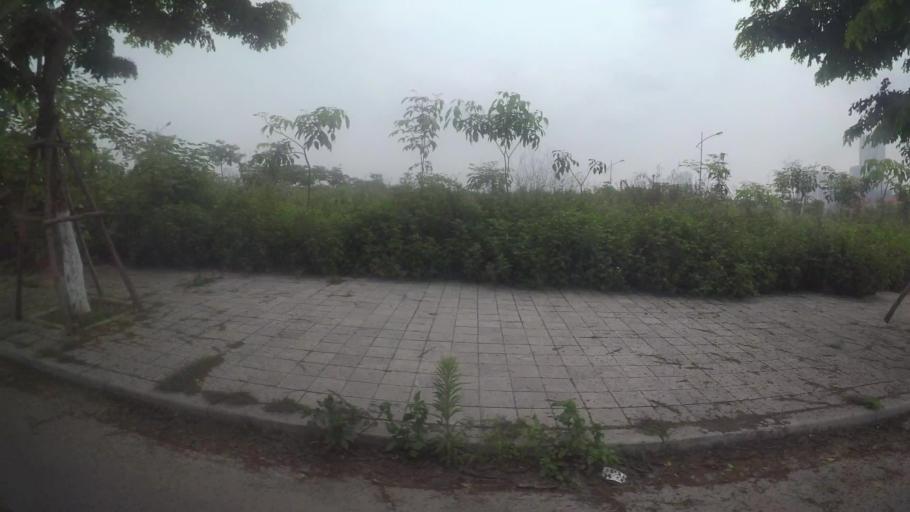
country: VN
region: Ha Noi
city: Ha Dong
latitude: 20.9777
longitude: 105.7527
